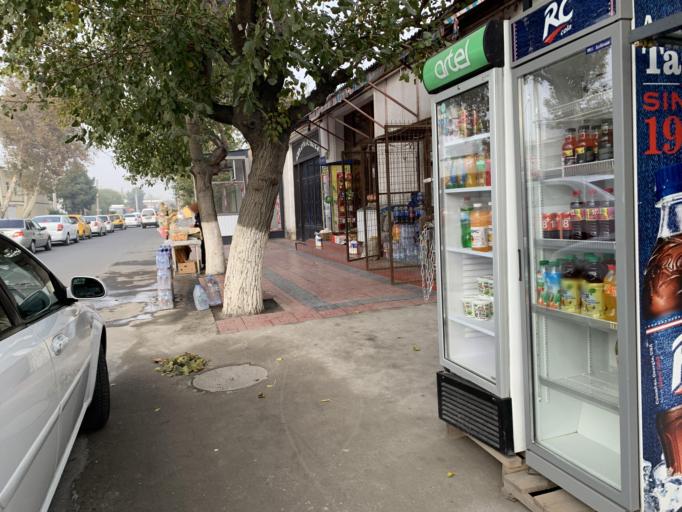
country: UZ
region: Fergana
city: Qo`qon
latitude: 40.5433
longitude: 70.9516
